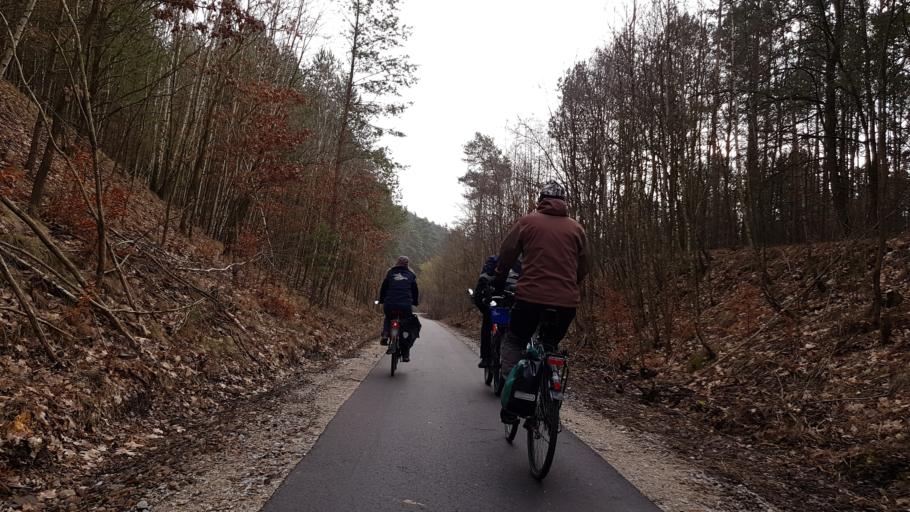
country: PL
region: West Pomeranian Voivodeship
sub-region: Powiat mysliborski
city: Barlinek
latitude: 53.0093
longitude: 15.2413
